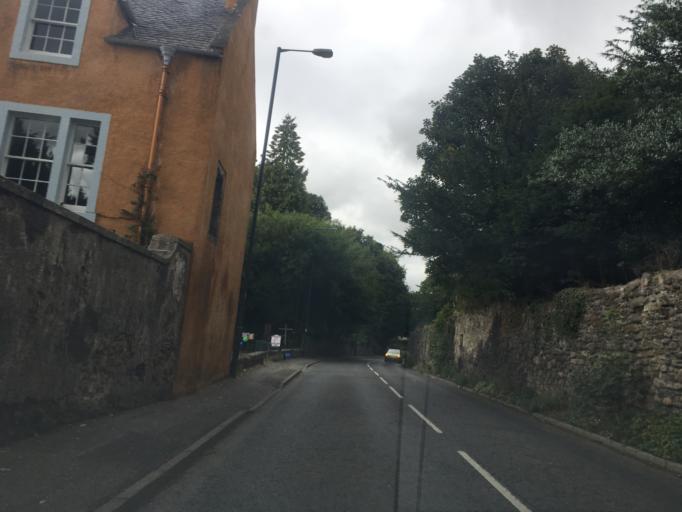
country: GB
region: Scotland
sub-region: Midlothian
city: Dalkeith
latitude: 55.8826
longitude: -3.0708
